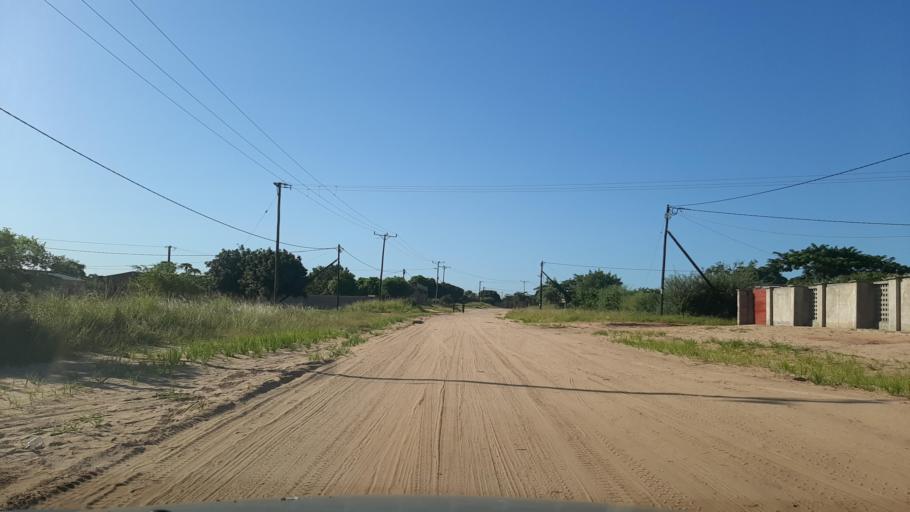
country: MZ
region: Maputo City
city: Maputo
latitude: -25.7659
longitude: 32.5474
